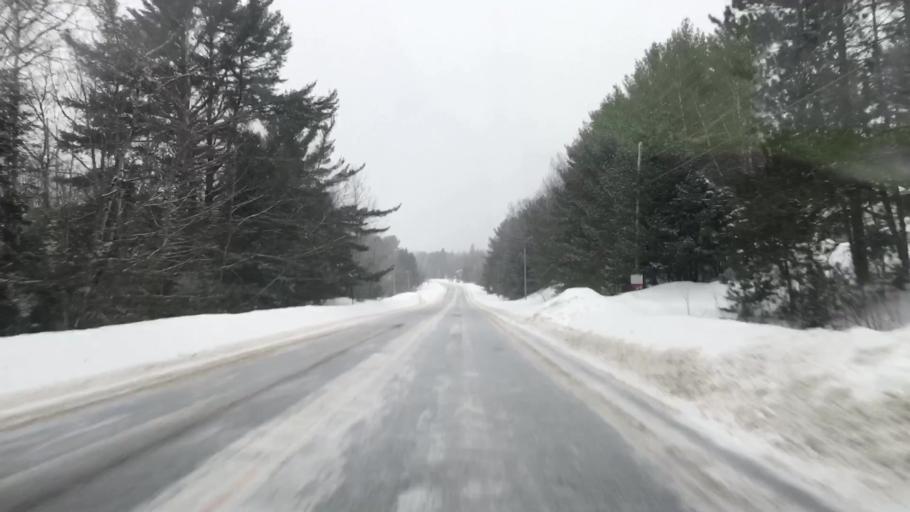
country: US
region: Maine
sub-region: Penobscot County
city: Medway
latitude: 45.5399
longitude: -68.3680
